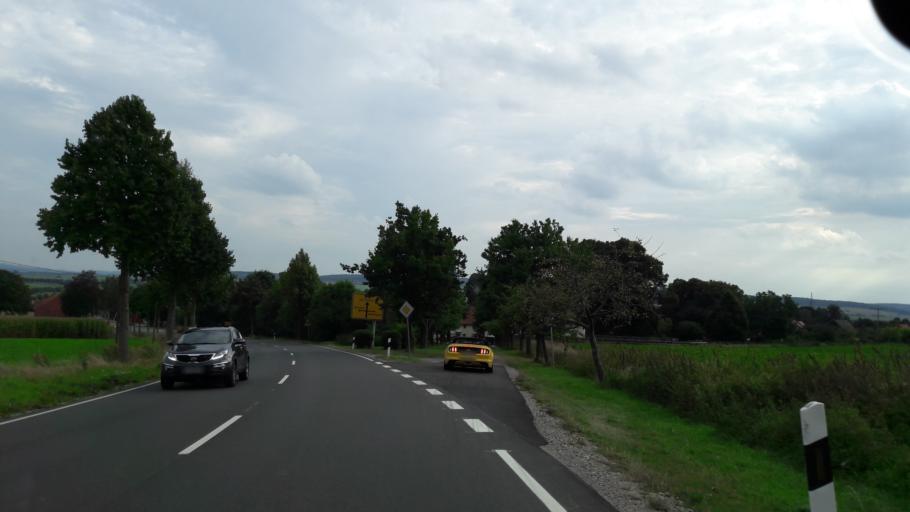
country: DE
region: Lower Saxony
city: Bockenem
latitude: 52.0406
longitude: 10.0842
